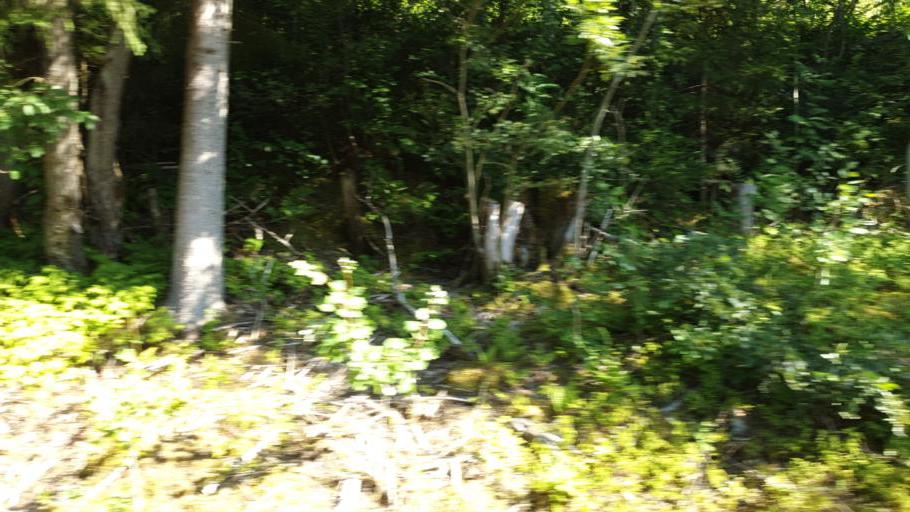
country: NO
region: Sor-Trondelag
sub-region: Orkdal
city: Orkanger
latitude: 63.1831
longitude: 9.7702
